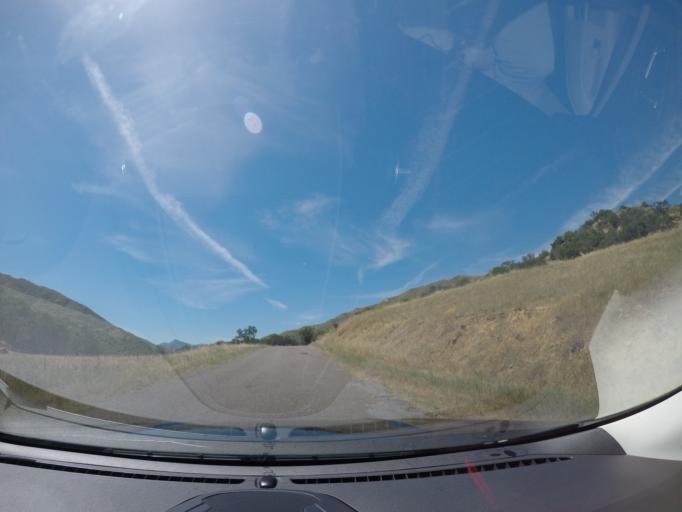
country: US
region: California
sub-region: Monterey County
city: King City
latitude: 35.9828
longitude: -121.3495
